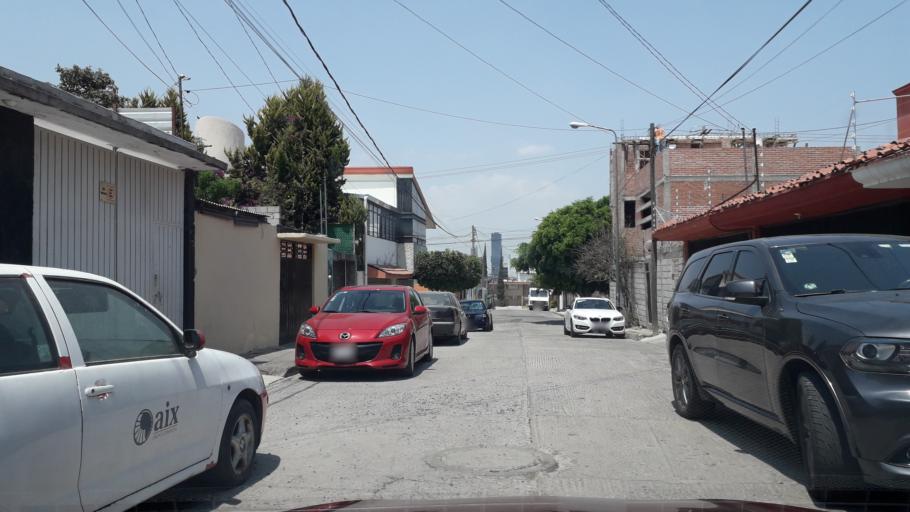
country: MX
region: Puebla
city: Puebla
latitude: 19.0534
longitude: -98.2349
